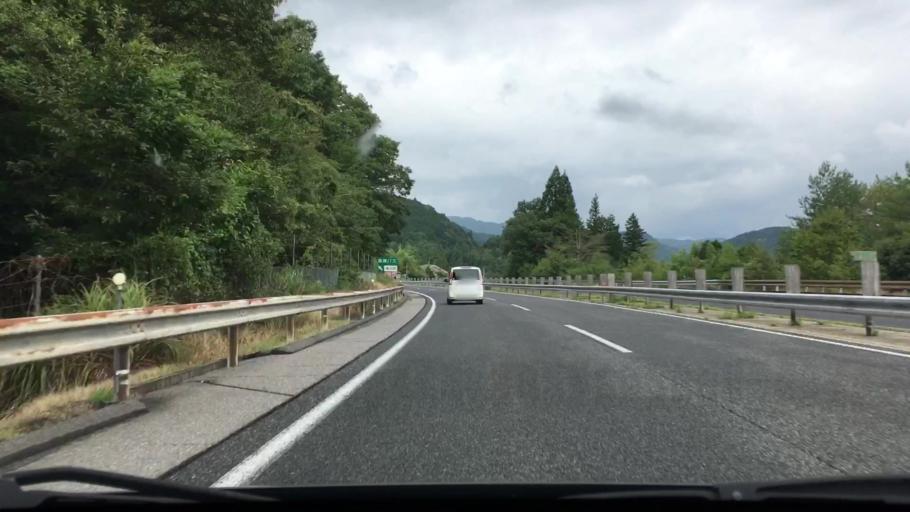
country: JP
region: Hiroshima
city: Miyoshi
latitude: 34.7182
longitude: 132.6651
